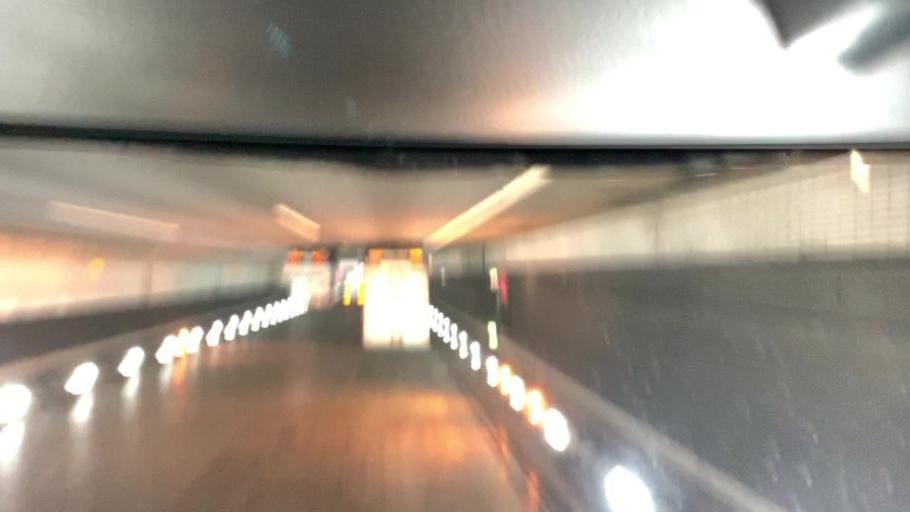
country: JP
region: Chiba
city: Nagareyama
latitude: 35.8924
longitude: 139.9167
